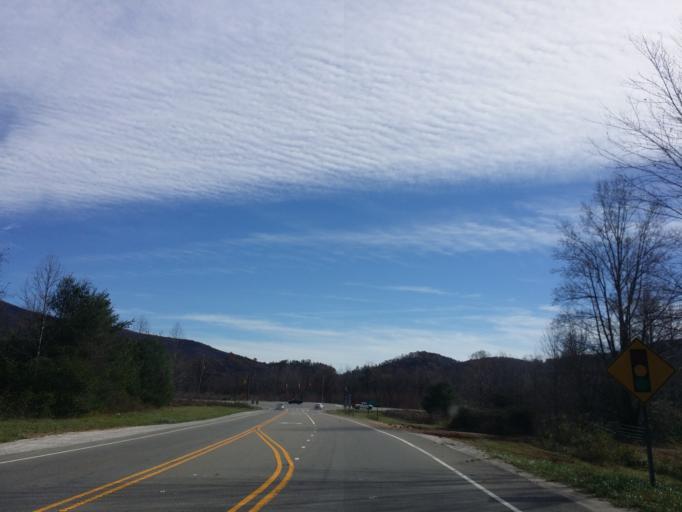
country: US
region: North Carolina
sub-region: McDowell County
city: Marion
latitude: 35.7989
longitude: -82.0346
